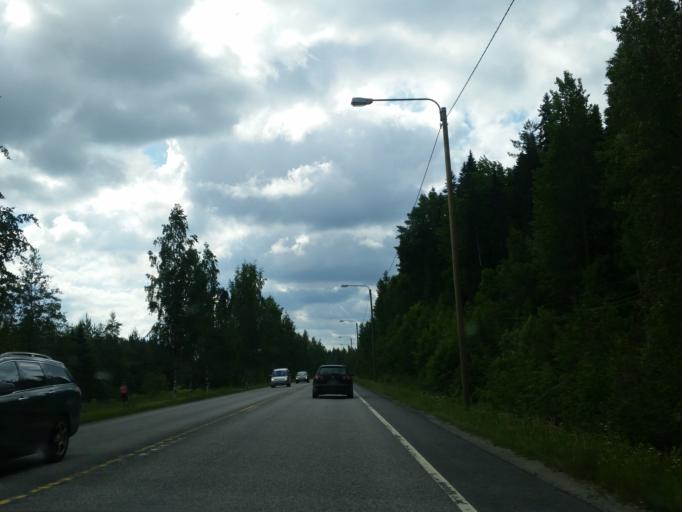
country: FI
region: Northern Savo
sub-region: Kuopio
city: Kuopio
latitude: 62.8466
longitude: 27.5493
